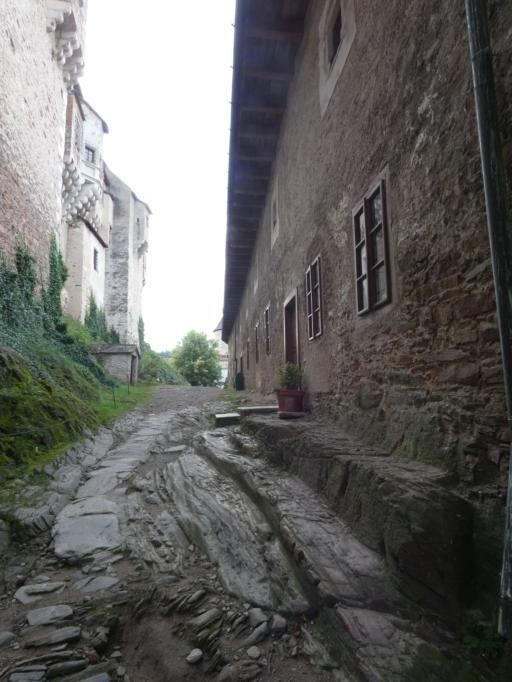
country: CZ
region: South Moravian
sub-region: Okres Brno-Venkov
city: Nedvedice
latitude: 49.4511
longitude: 16.3180
